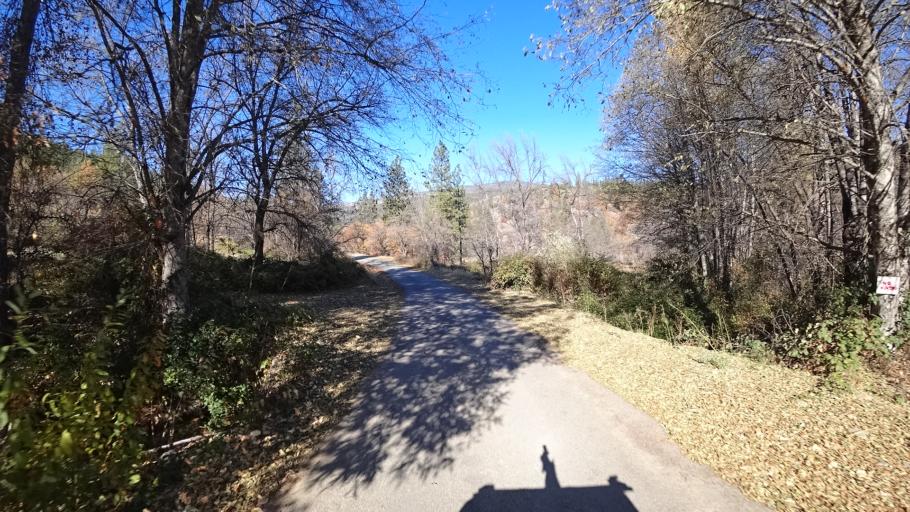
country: US
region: California
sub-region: Siskiyou County
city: Yreka
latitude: 41.8418
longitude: -122.8928
